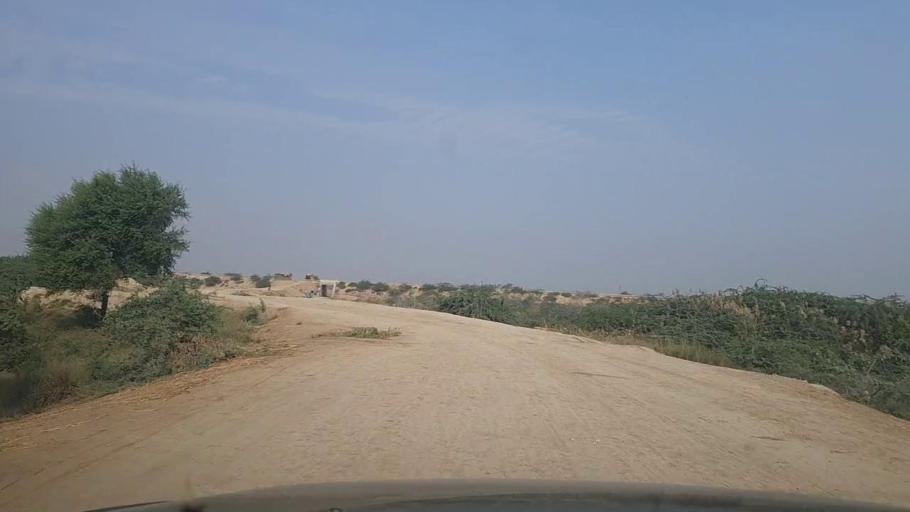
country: PK
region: Sindh
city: Bulri
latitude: 25.0323
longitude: 68.2796
